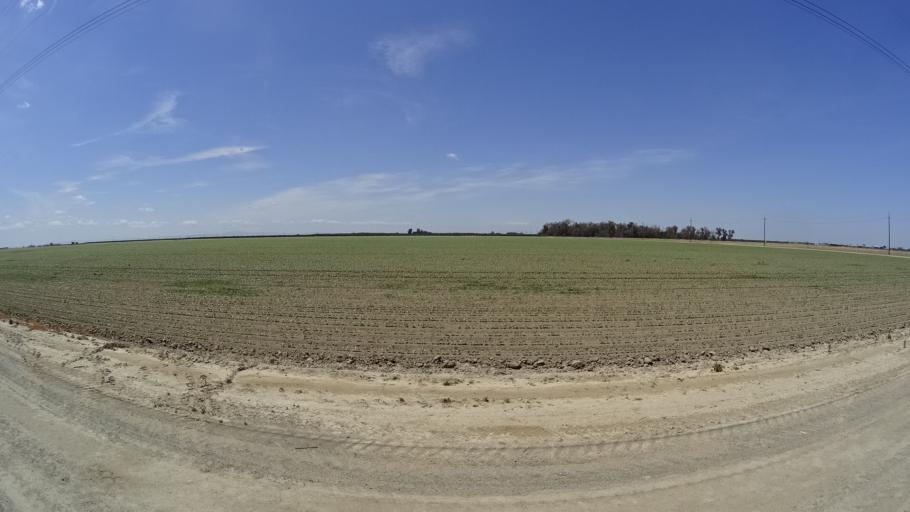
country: US
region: California
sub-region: Kings County
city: Home Garden
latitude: 36.2535
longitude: -119.6728
